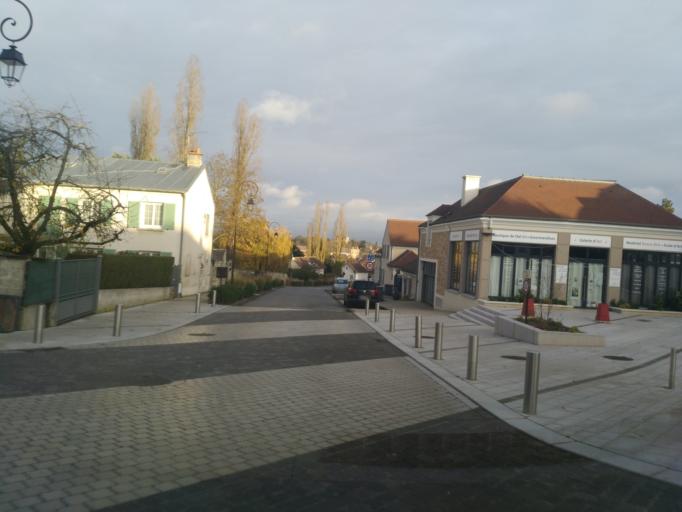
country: FR
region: Ile-de-France
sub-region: Departement des Yvelines
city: Fourqueux
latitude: 48.8873
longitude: 2.0634
